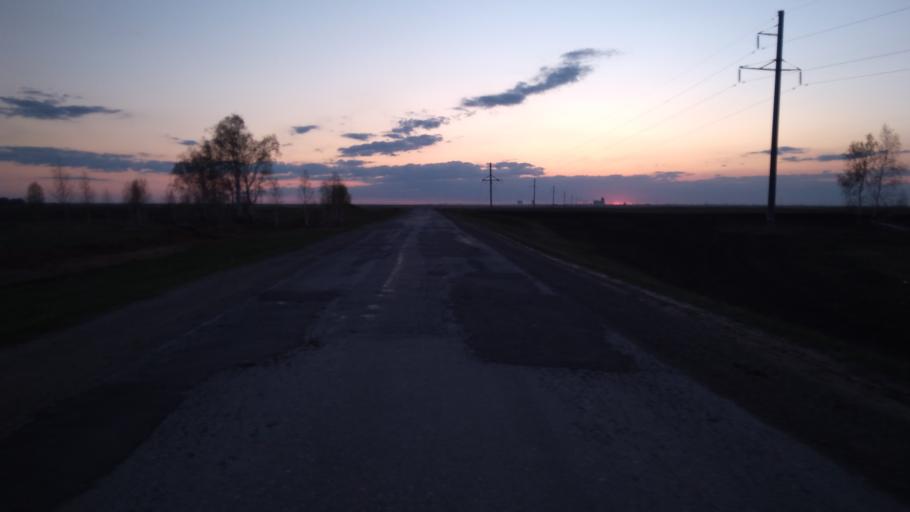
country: RU
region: Chelyabinsk
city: Bobrovka
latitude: 54.0862
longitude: 61.6657
